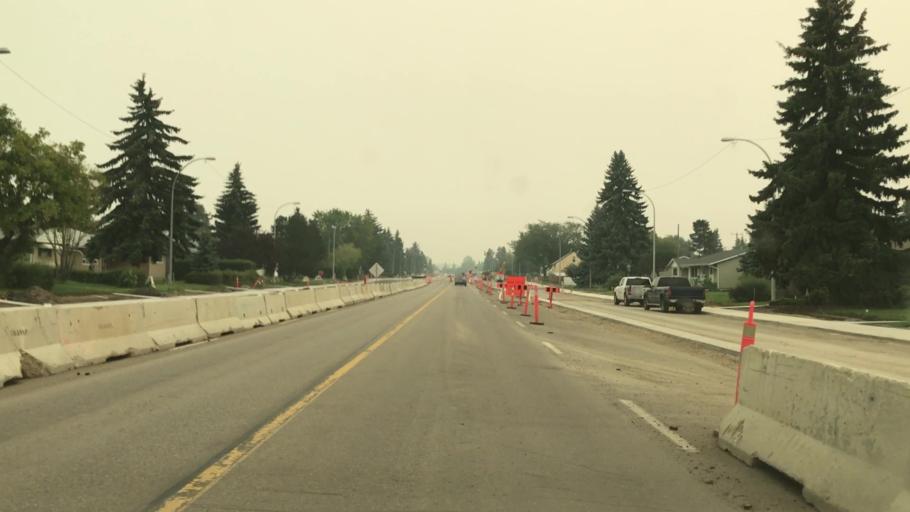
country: CA
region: Alberta
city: Edmonton
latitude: 53.5112
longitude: -113.4552
